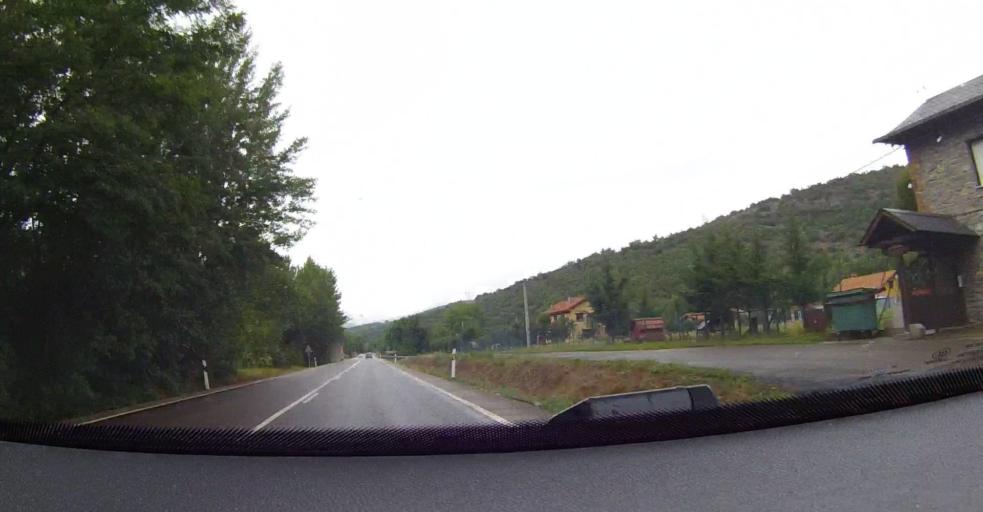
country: ES
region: Castille and Leon
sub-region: Provincia de Leon
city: Cistierna
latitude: 42.8260
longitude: -5.1207
